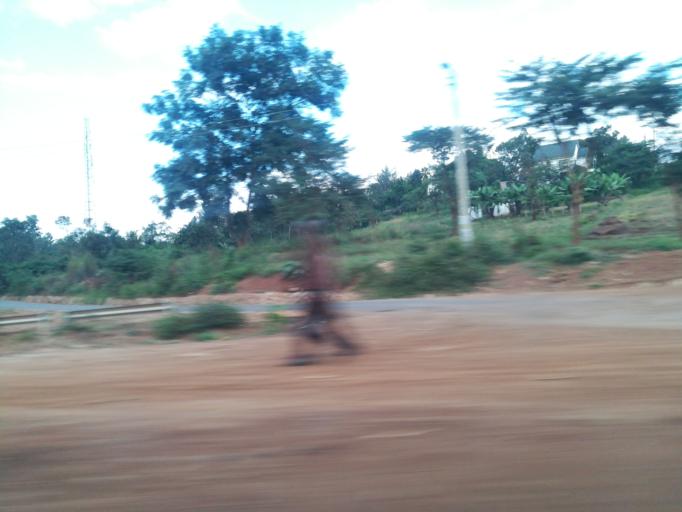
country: KE
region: Nairobi Area
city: Thika
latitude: -1.0274
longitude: 37.0652
